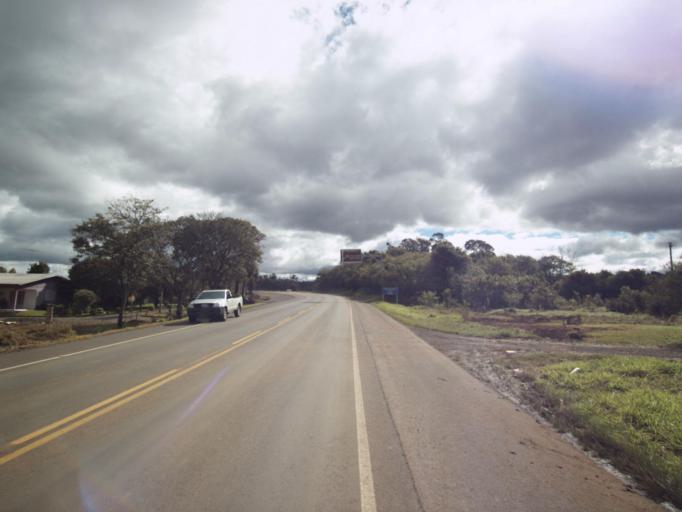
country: BR
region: Santa Catarina
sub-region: Concordia
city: Concordia
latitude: -27.3291
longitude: -51.9782
